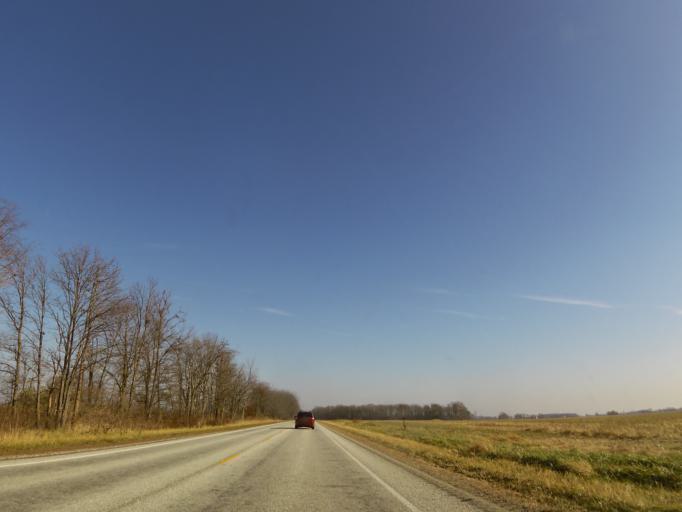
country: US
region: Indiana
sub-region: Shelby County
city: Morristown
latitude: 39.5606
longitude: -85.6551
